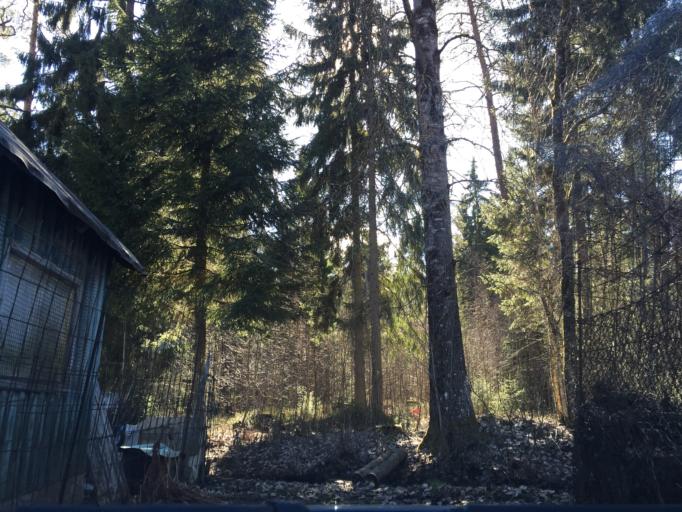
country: LV
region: Incukalns
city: Vangazi
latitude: 57.0904
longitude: 24.5327
